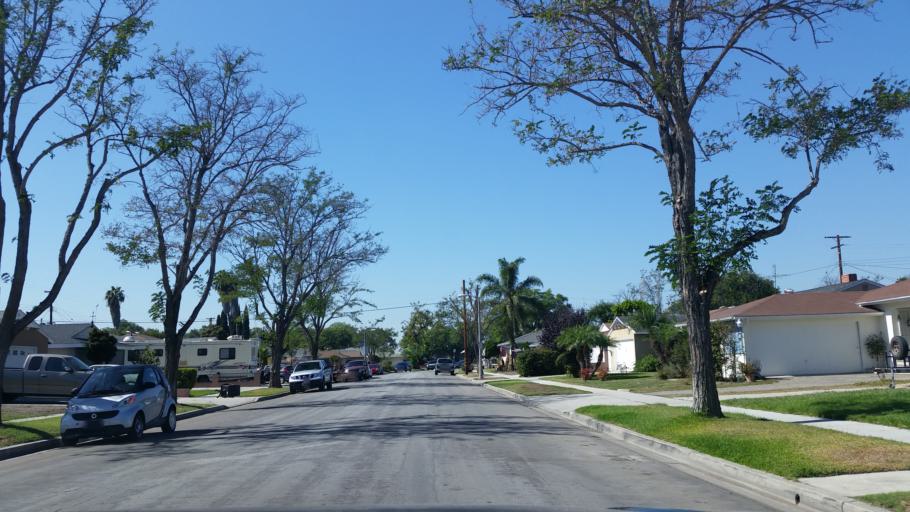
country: US
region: California
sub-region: Los Angeles County
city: Lakewood
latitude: 33.8678
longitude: -118.1489
